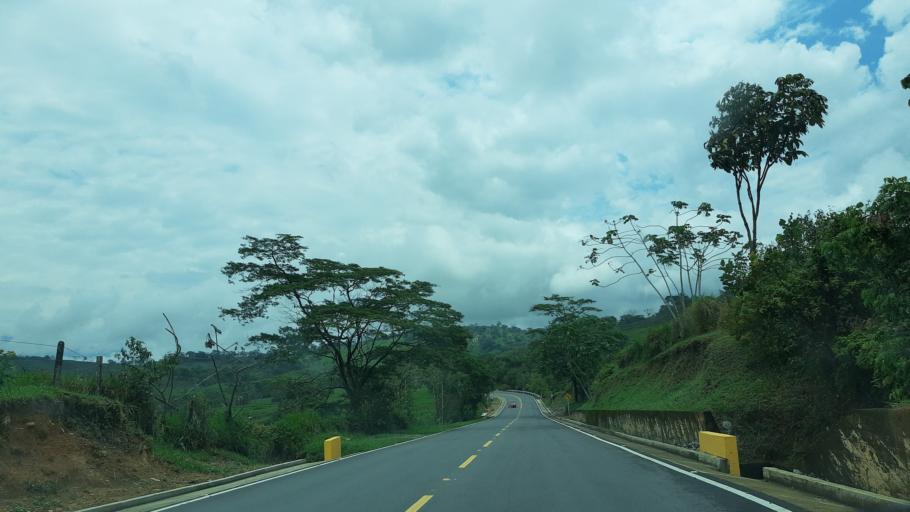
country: CO
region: Casanare
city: Sabanalarga
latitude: 4.8074
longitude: -73.0599
